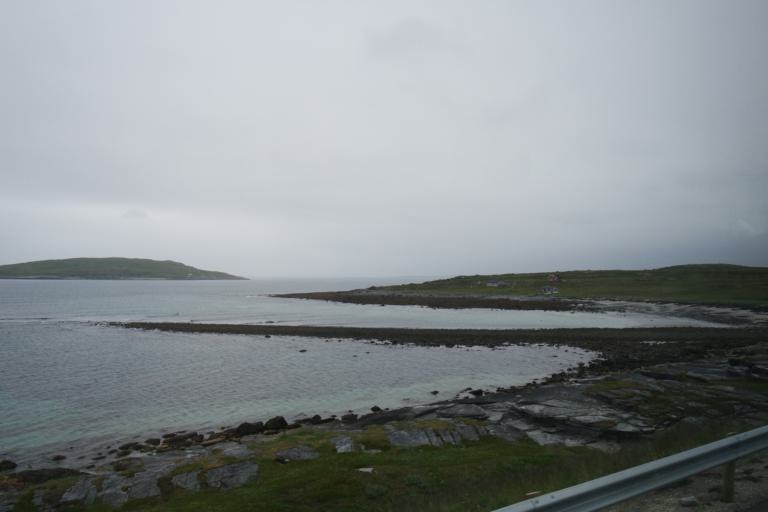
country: NO
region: Finnmark Fylke
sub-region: Nordkapp
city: Honningsvag
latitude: 70.8299
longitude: 25.7771
